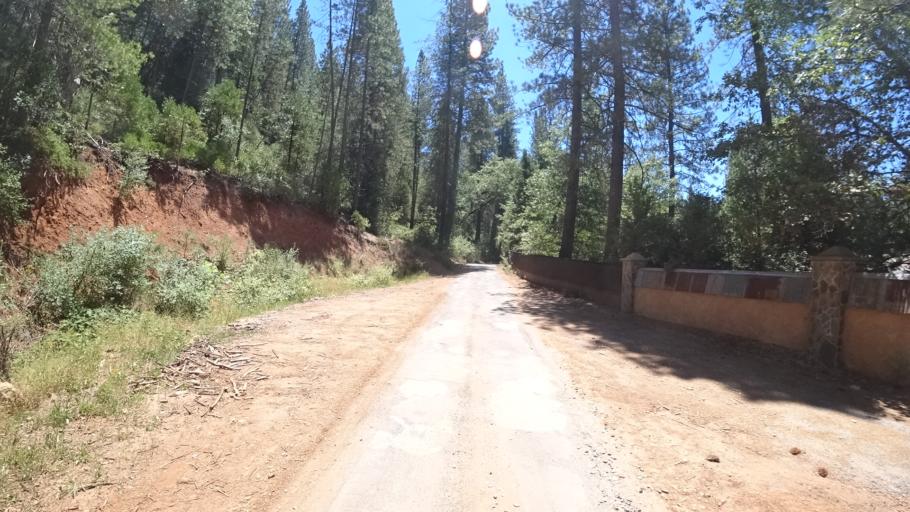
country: US
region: California
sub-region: Calaveras County
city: Arnold
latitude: 38.2604
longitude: -120.4116
